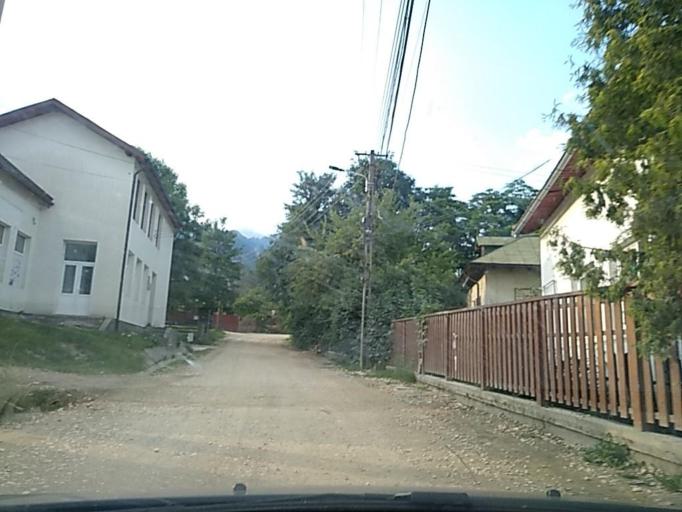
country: RO
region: Brasov
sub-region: Comuna Bran
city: Simon
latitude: 45.5023
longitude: 25.3829
